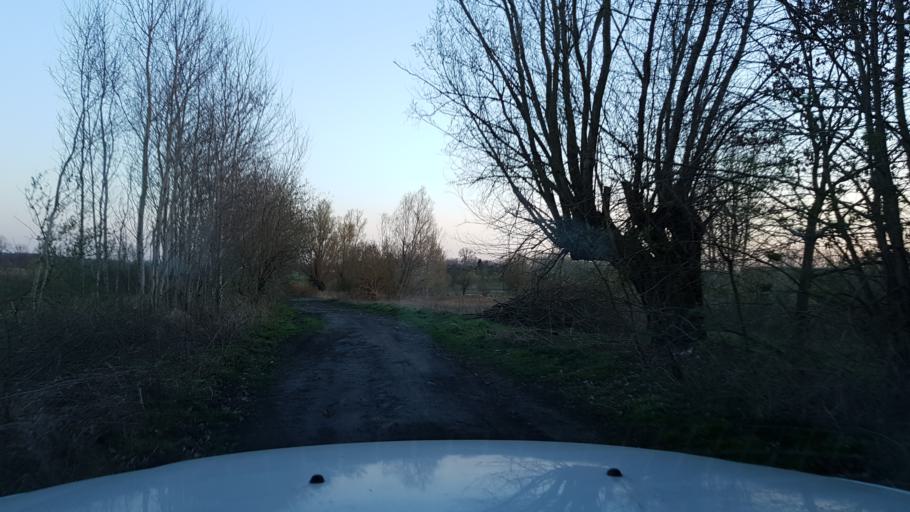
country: PL
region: West Pomeranian Voivodeship
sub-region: Powiat bialogardzki
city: Bialogard
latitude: 53.9743
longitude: 15.9567
